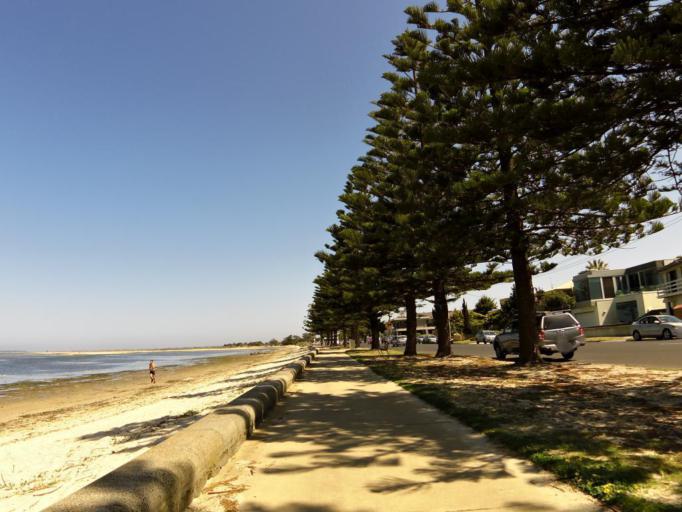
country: AU
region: Victoria
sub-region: Hobsons Bay
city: Altona
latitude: -37.8741
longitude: 144.8161
